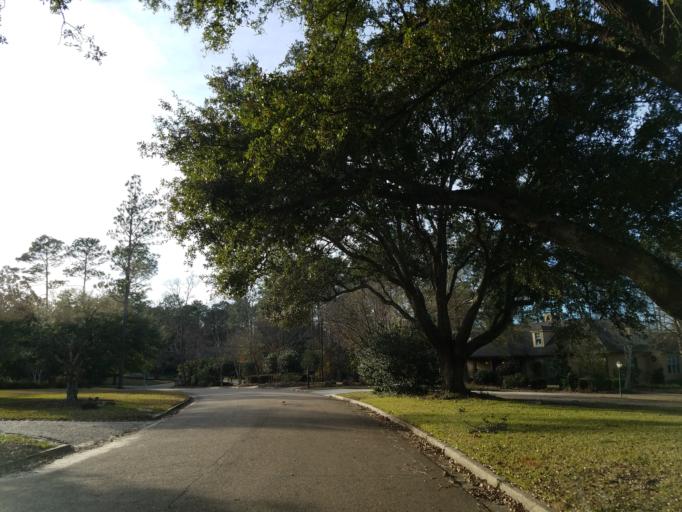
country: US
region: Mississippi
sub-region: Lamar County
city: West Hattiesburg
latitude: 31.3095
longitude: -89.3453
